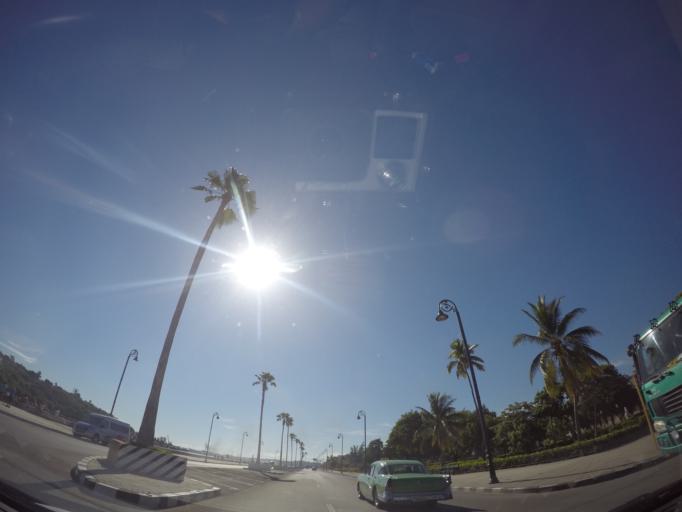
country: CU
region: La Habana
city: La Habana Vieja
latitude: 23.1431
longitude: -82.3517
